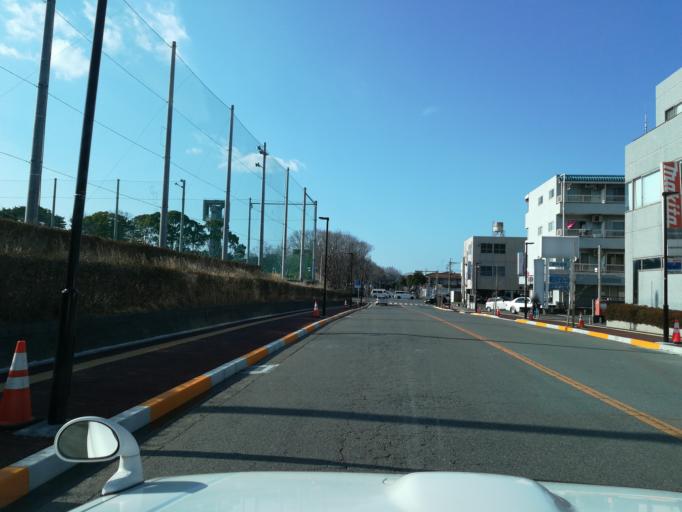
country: JP
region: Ibaraki
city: Naka
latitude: 36.0892
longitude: 140.1098
